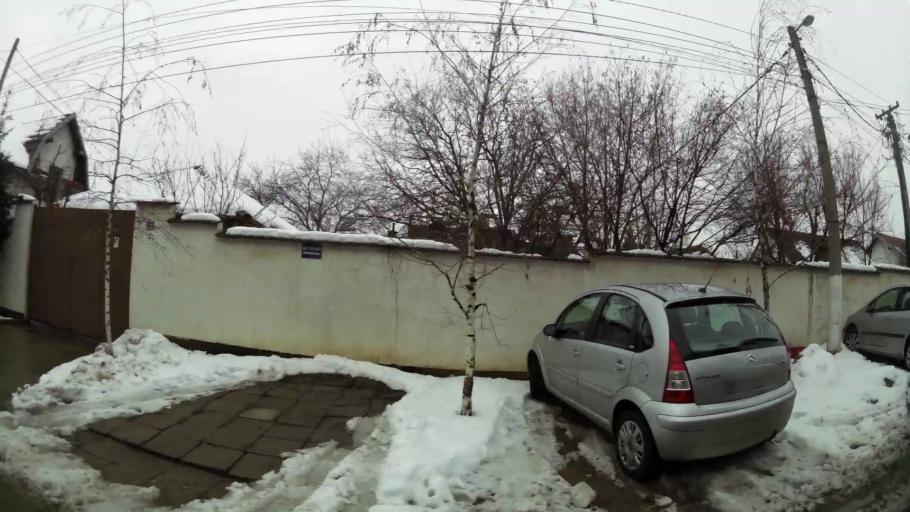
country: RS
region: Central Serbia
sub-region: Belgrade
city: Zemun
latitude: 44.8318
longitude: 20.3807
